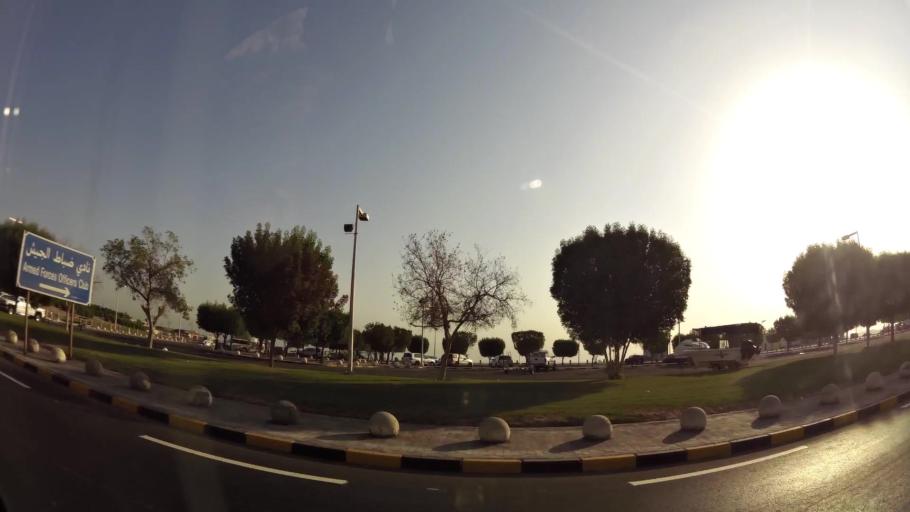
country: KW
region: Al Asimah
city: Ad Dasmah
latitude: 29.3760
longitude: 48.0048
